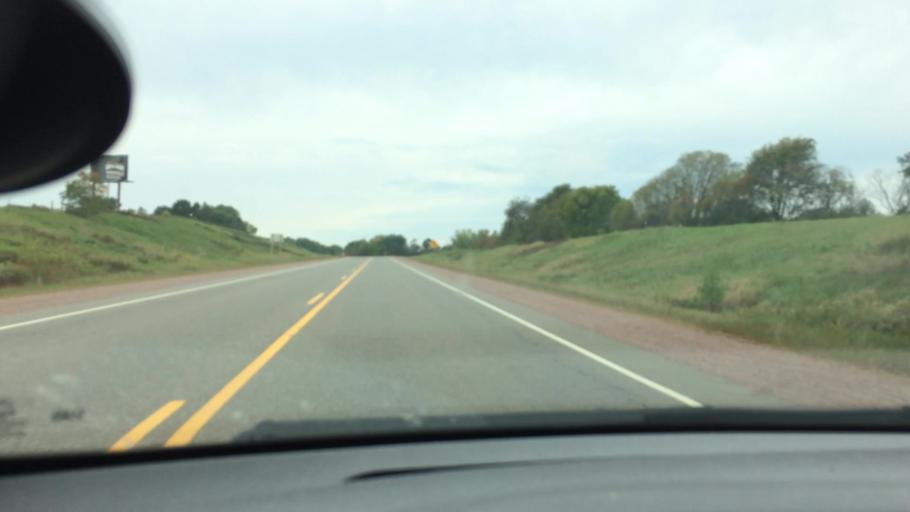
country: US
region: Wisconsin
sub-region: Clark County
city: Neillsville
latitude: 44.5522
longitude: -90.6143
